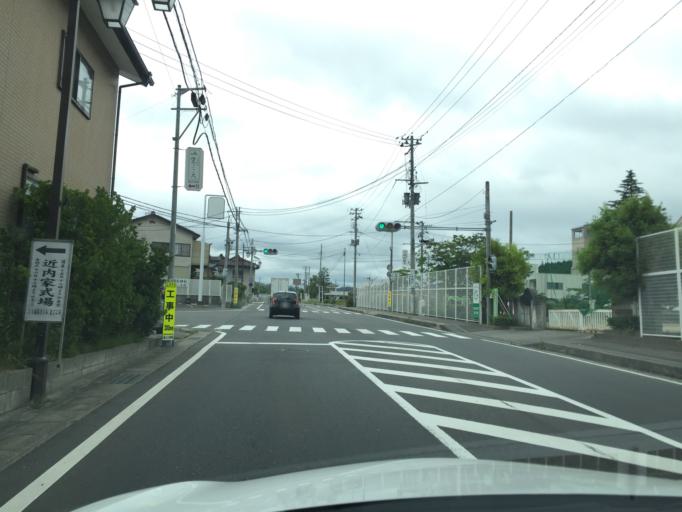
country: JP
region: Fukushima
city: Funehikimachi-funehiki
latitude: 37.4372
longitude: 140.5801
